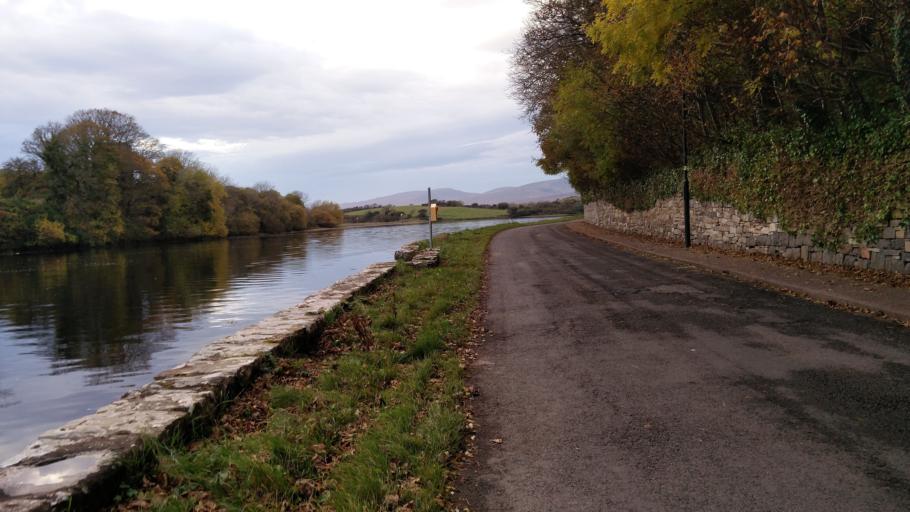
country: IE
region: Connaught
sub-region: Maigh Eo
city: Westport
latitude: 53.8845
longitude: -9.5549
